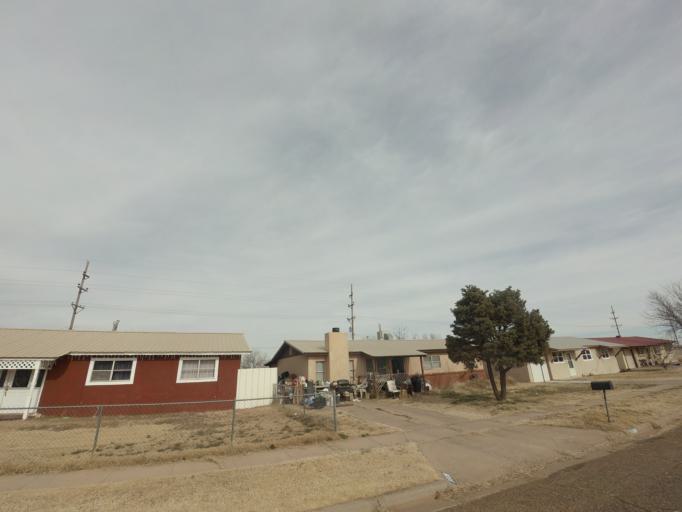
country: US
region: New Mexico
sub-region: Curry County
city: Clovis
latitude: 34.4115
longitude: -103.2432
